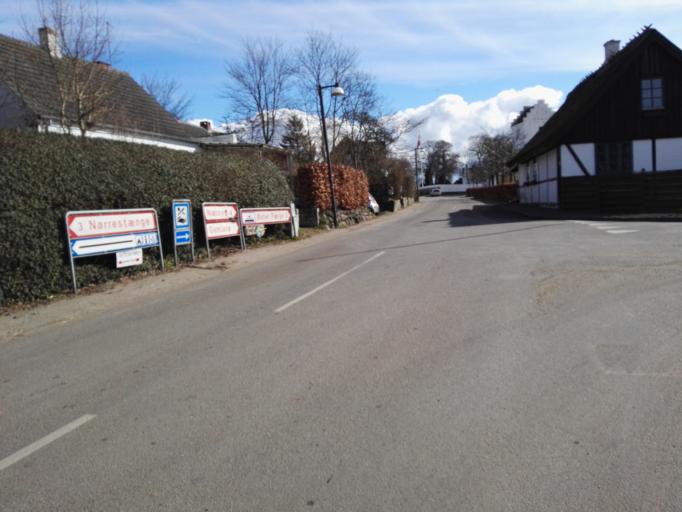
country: DK
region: Zealand
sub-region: Lejre Kommune
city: Ejby
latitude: 55.7671
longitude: 11.8060
